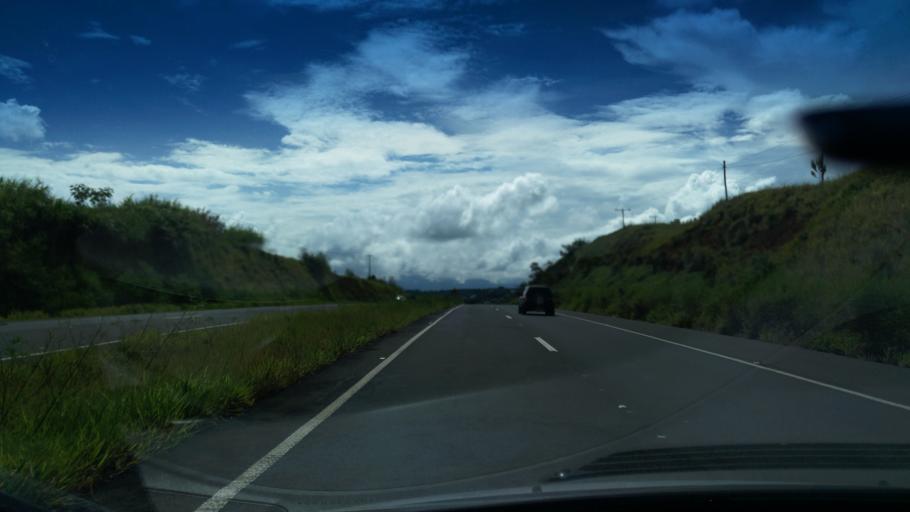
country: BR
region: Sao Paulo
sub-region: Santo Antonio Do Jardim
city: Espirito Santo do Pinhal
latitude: -22.1710
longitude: -46.7435
